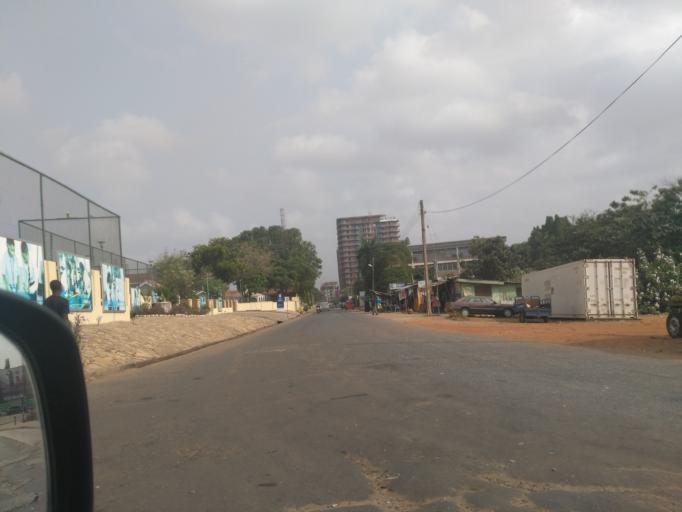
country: GH
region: Greater Accra
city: Accra
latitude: 5.6093
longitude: -0.1779
